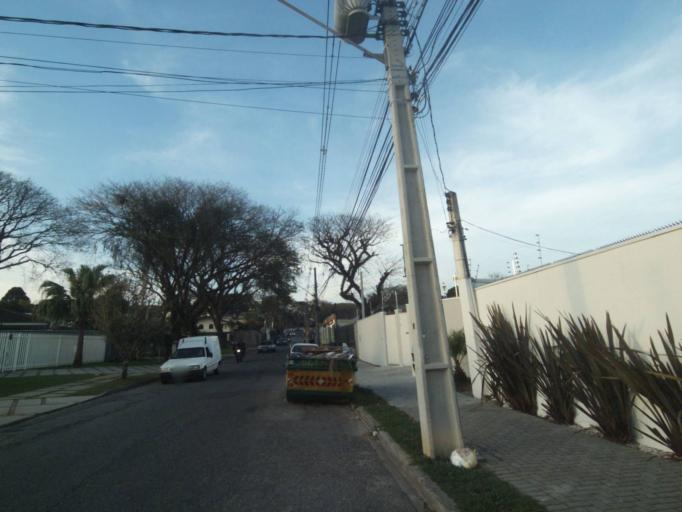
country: BR
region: Parana
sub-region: Curitiba
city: Curitiba
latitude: -25.4535
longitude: -49.3110
